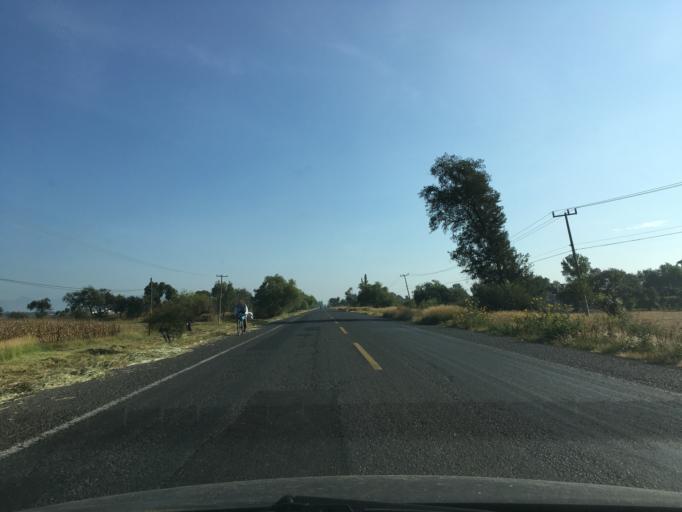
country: MX
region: Michoacan
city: Alvaro Obregon
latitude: 19.8310
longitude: -101.0359
